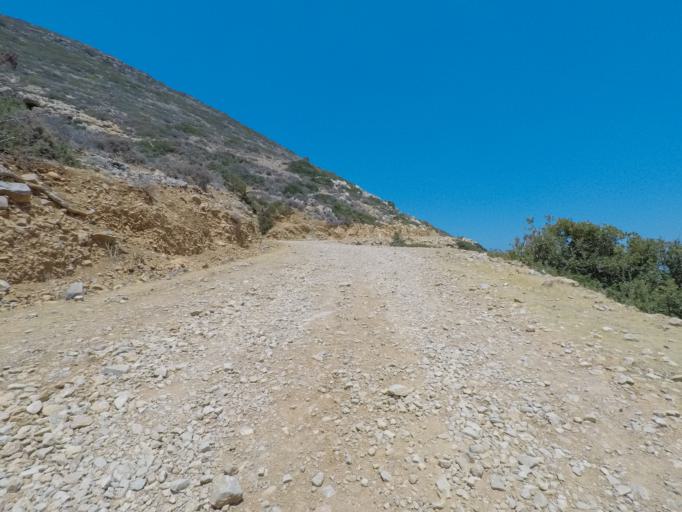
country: GR
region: Crete
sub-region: Nomos Lasithiou
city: Elounda
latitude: 35.3131
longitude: 25.7470
